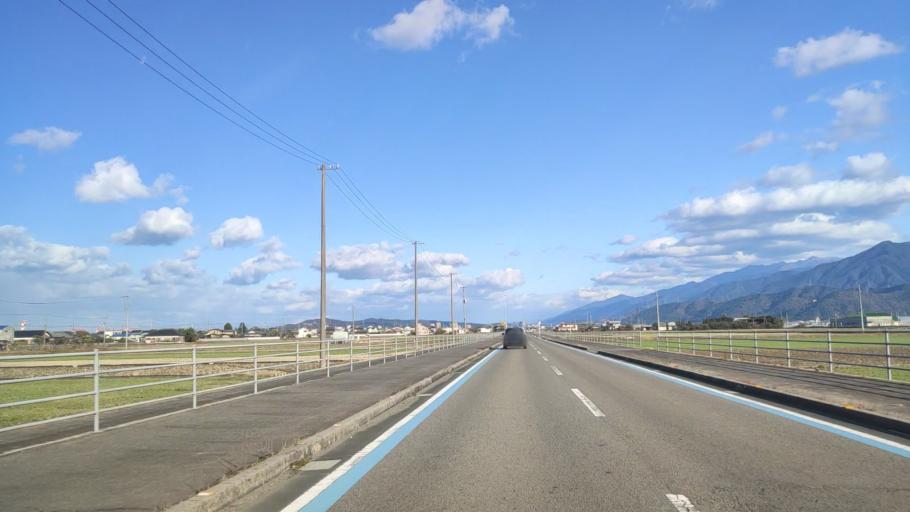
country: JP
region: Ehime
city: Saijo
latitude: 33.9077
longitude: 133.1483
